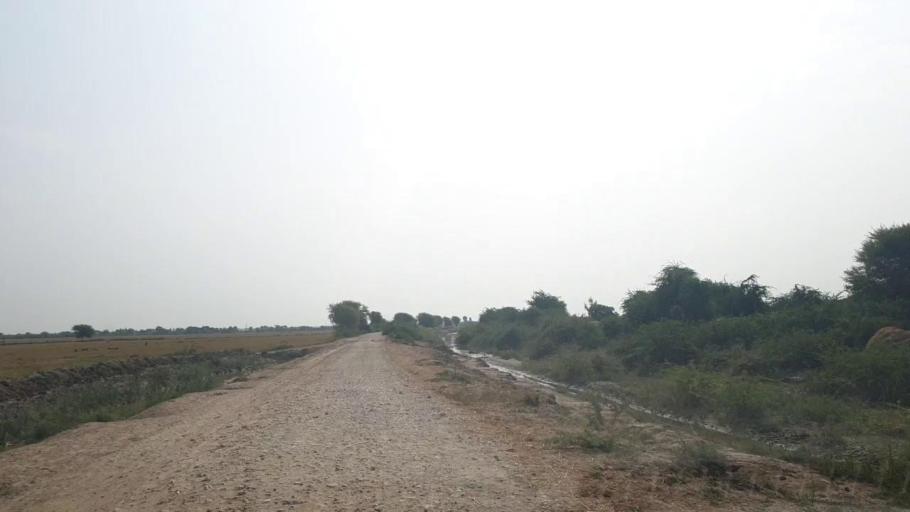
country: PK
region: Sindh
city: Badin
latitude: 24.7601
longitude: 68.7585
